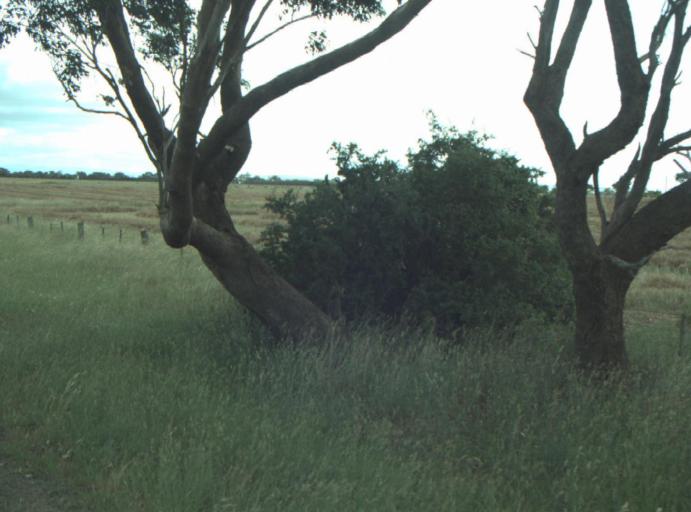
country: AU
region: Victoria
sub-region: Greater Geelong
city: Lara
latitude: -37.8582
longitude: 144.3522
